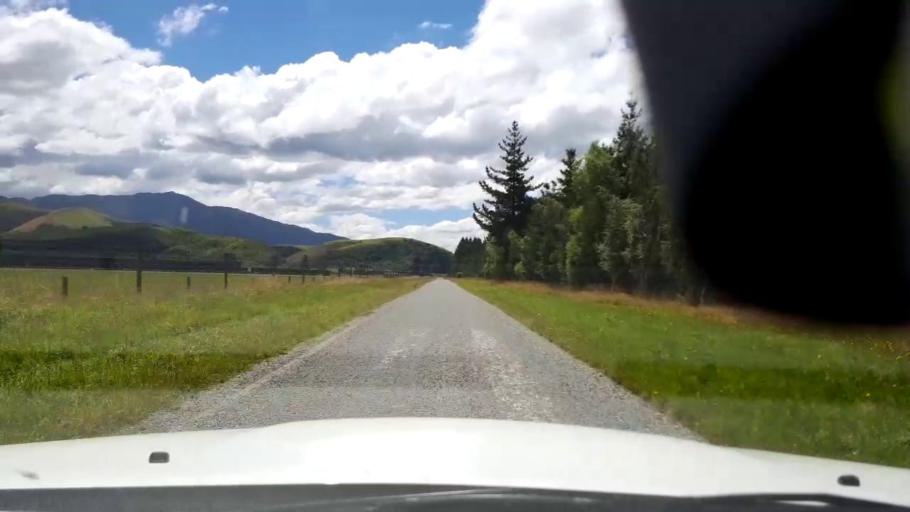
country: NZ
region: Canterbury
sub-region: Timaru District
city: Pleasant Point
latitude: -43.9657
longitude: 171.2267
